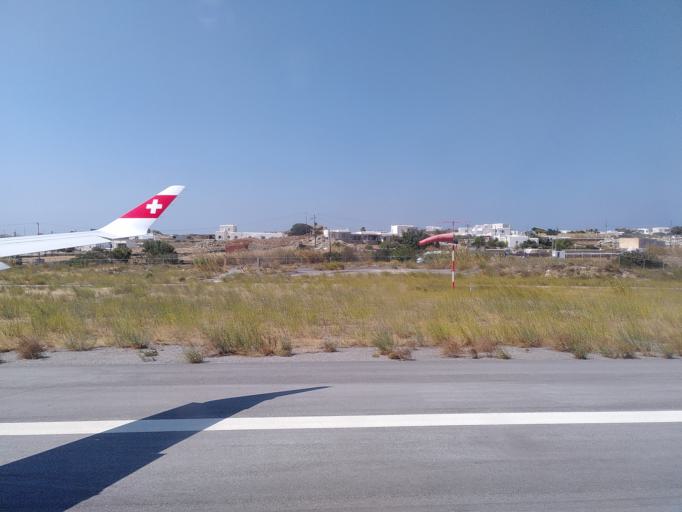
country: GR
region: South Aegean
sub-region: Nomos Kykladon
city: Mykonos
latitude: 37.4303
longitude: 25.3504
